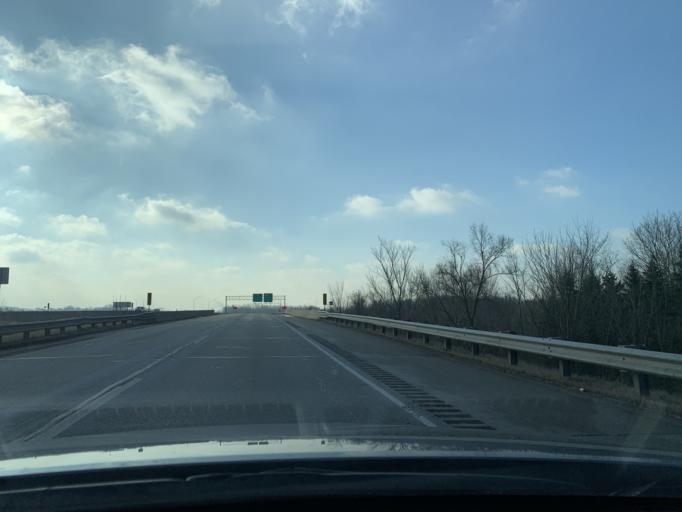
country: US
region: Indiana
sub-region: Porter County
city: Valparaiso
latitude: 41.4771
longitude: -87.0205
